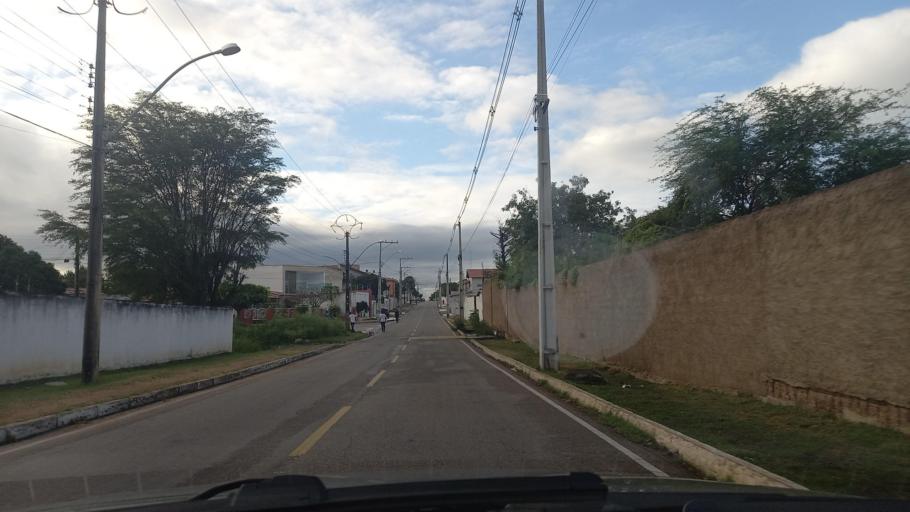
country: BR
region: Bahia
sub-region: Paulo Afonso
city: Paulo Afonso
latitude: -9.3937
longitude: -38.2318
